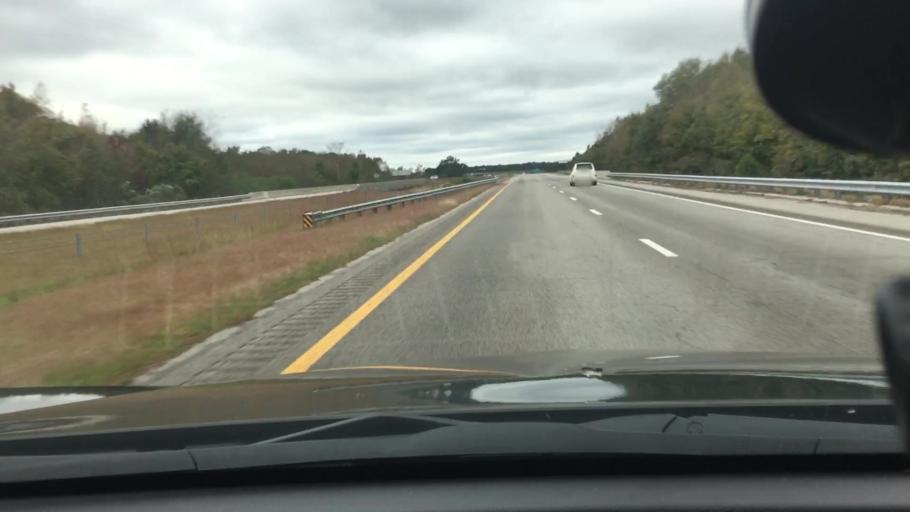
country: US
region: North Carolina
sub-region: Wilson County
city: Wilson
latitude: 35.6715
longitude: -77.8933
